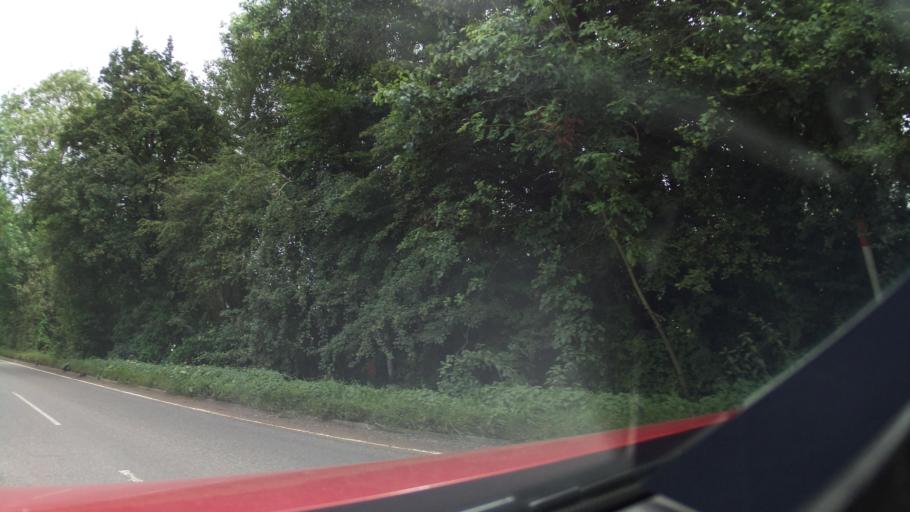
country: GB
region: England
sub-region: Northamptonshire
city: Corby
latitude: 52.5118
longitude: -0.6831
